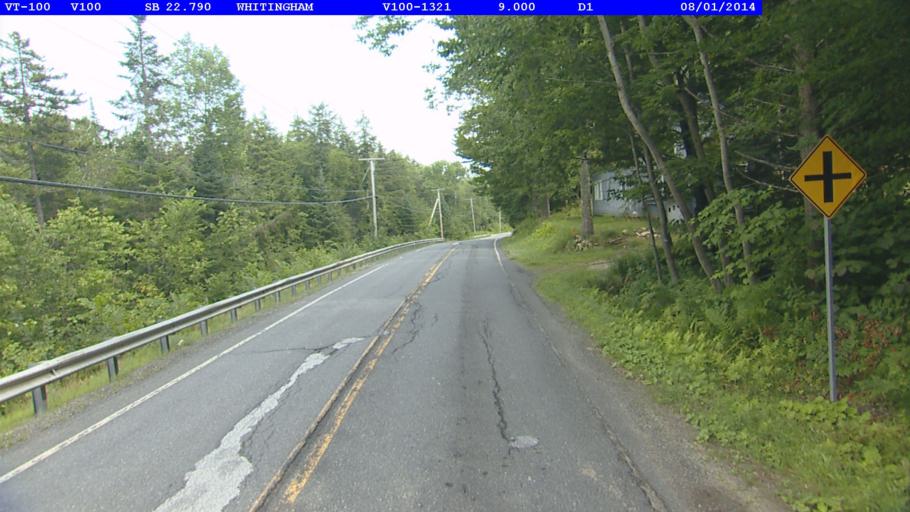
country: US
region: Vermont
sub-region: Windham County
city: Dover
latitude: 42.8094
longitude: -72.8399
